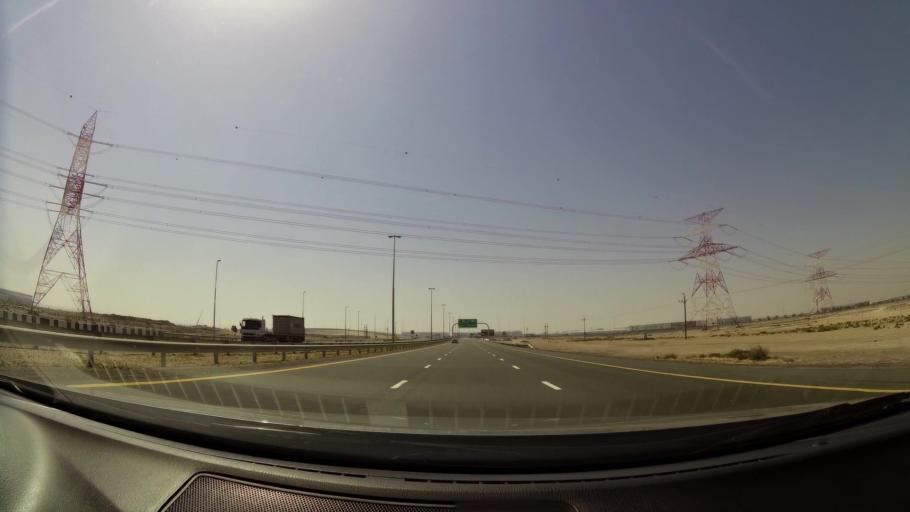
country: AE
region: Dubai
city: Dubai
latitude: 24.9229
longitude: 55.0985
